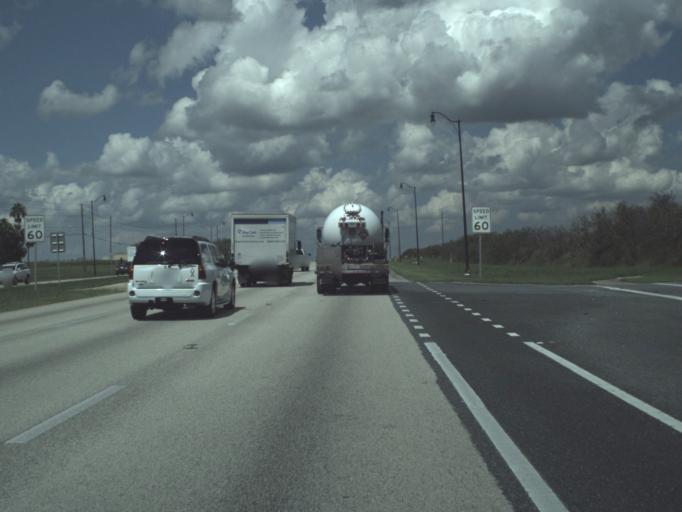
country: US
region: Florida
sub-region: Polk County
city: Davenport
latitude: 28.1809
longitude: -81.6397
